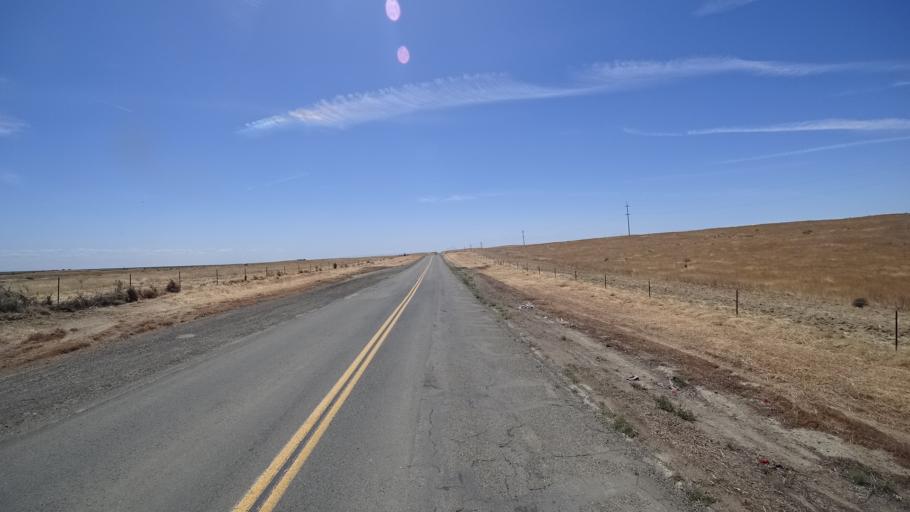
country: US
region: California
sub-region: Kings County
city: Kettleman City
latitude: 35.9047
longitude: -119.9150
